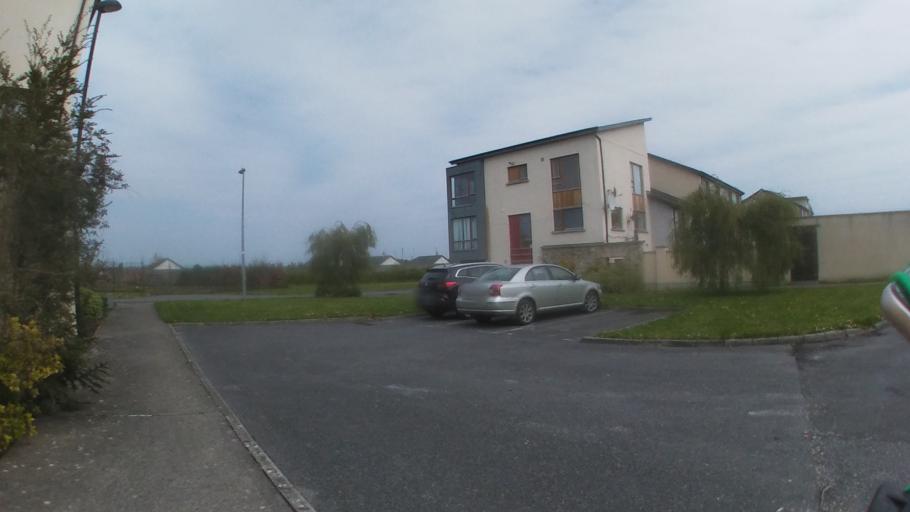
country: IE
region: Leinster
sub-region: Kilkenny
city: Kilkenny
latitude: 52.6407
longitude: -7.2701
